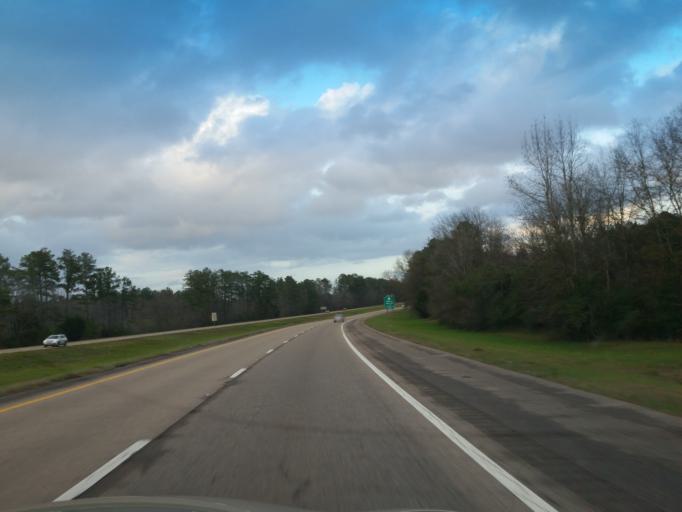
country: US
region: Mississippi
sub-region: Clarke County
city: Stonewall
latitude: 32.0453
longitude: -88.9191
